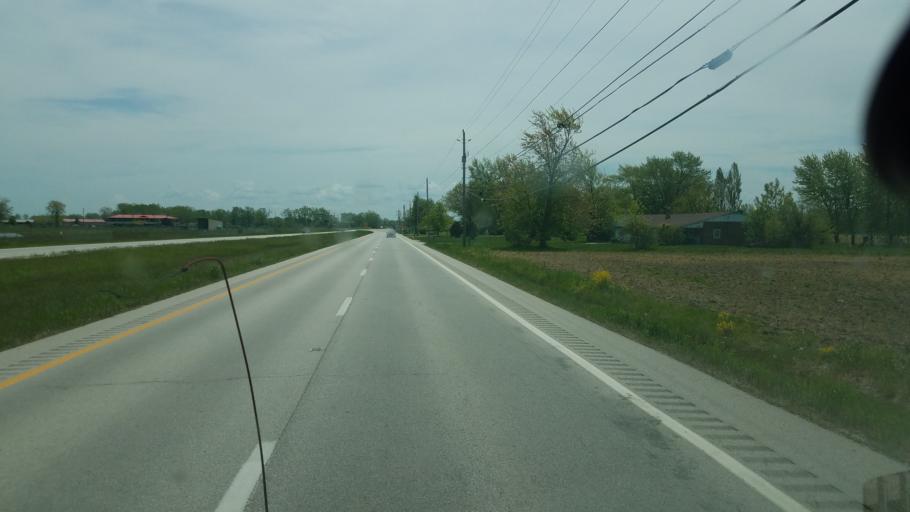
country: US
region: Ohio
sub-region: Ottawa County
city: Port Clinton
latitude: 41.5328
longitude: -83.0257
